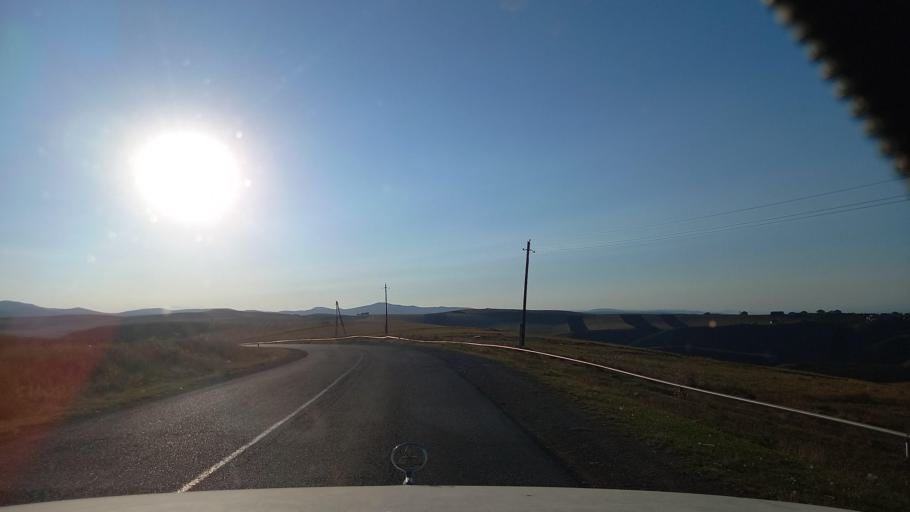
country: AZ
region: Shamkir Rayon
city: Shamkhor
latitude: 40.7662
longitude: 45.9392
